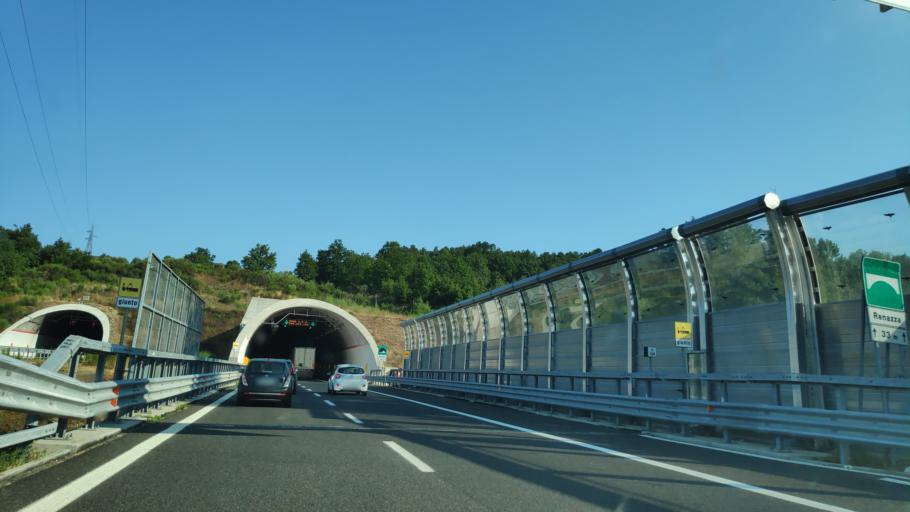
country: IT
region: Basilicate
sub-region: Provincia di Potenza
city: Lagonegro
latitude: 40.1389
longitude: 15.7585
